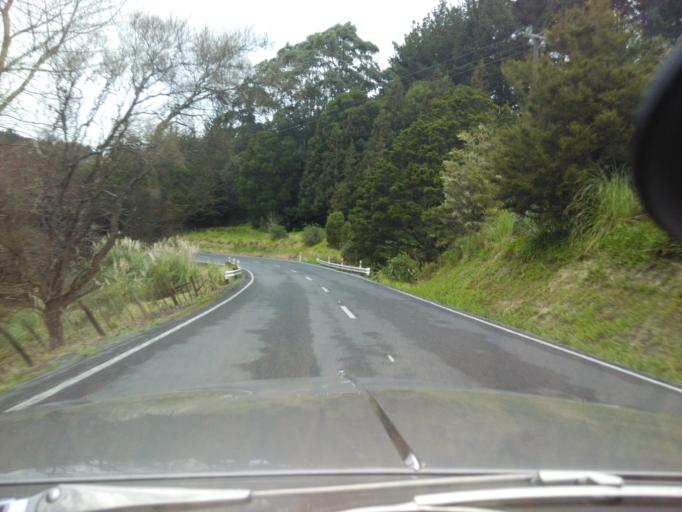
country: NZ
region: Auckland
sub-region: Auckland
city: Warkworth
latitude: -36.5039
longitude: 174.6393
